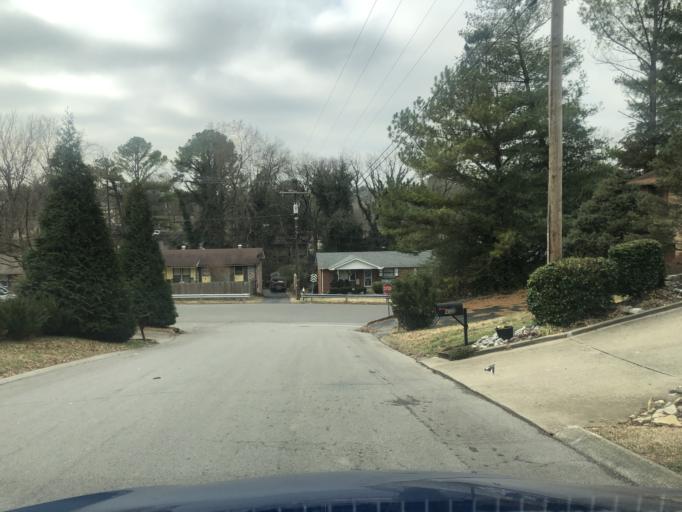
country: US
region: Tennessee
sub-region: Davidson County
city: Oak Hill
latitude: 36.0924
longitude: -86.7149
